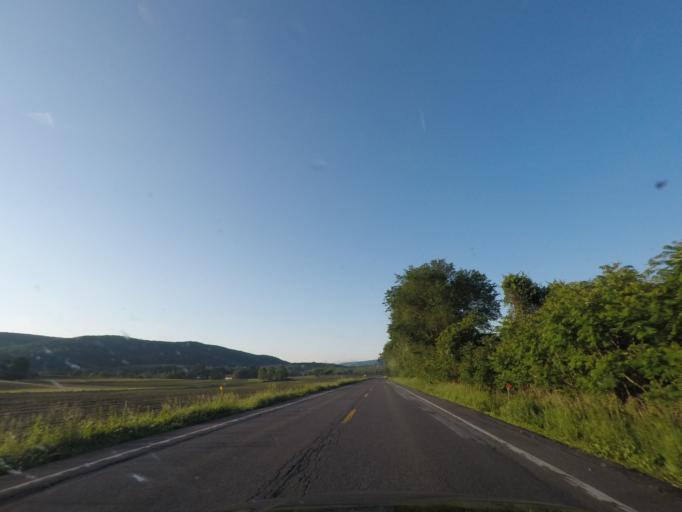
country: US
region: New York
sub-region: Dutchess County
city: Pine Plains
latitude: 41.9996
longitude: -73.5229
